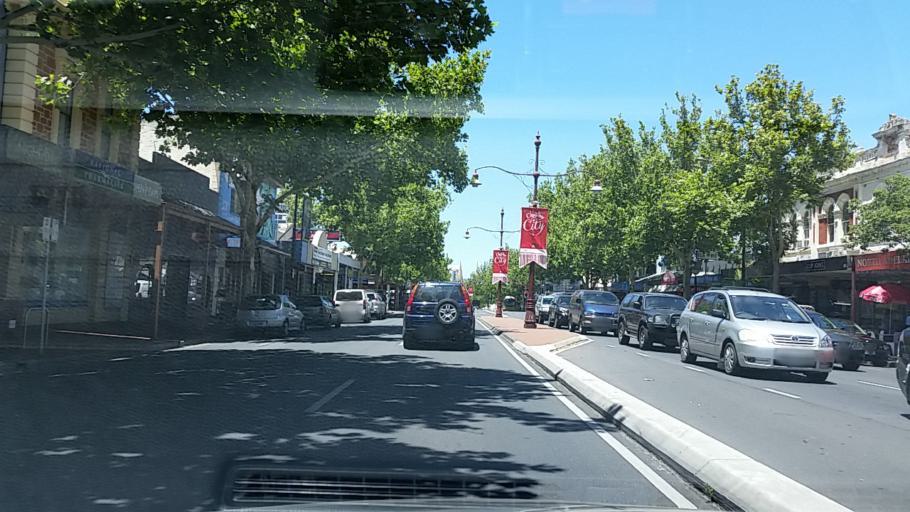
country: AU
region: South Australia
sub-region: Adelaide
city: North Adelaide
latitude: -34.9074
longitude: 138.5964
